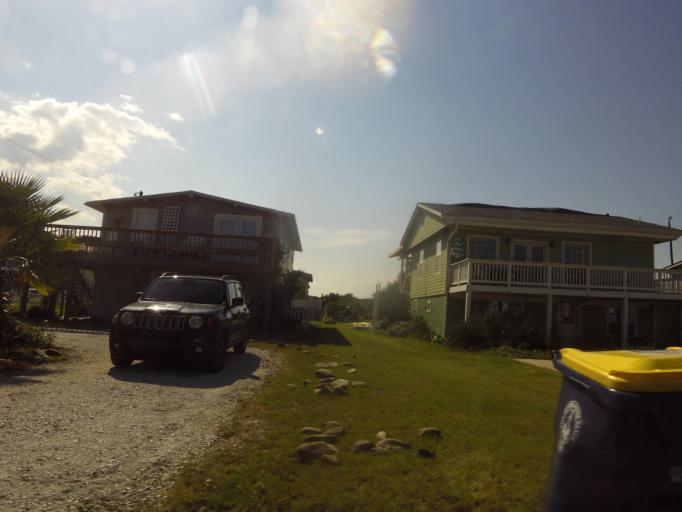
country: US
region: Florida
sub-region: Nassau County
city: Fernandina Beach
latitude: 30.6801
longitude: -81.4300
